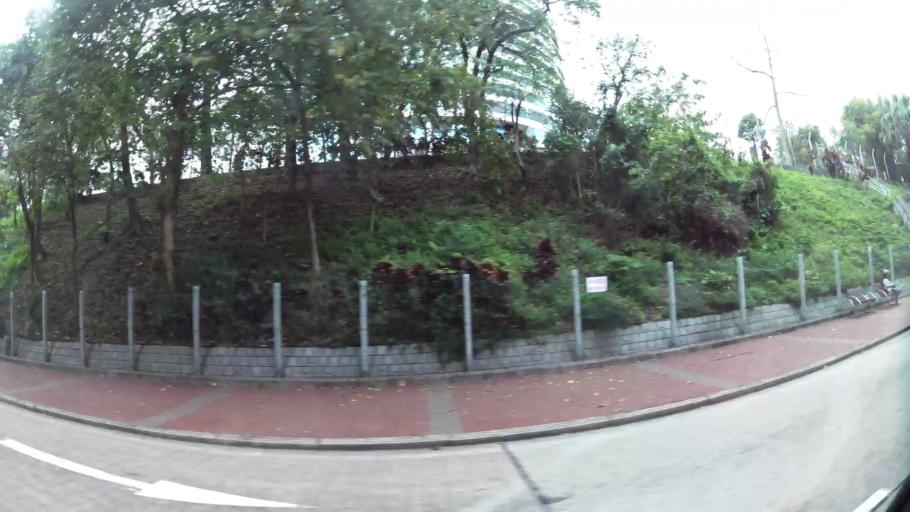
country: HK
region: Sham Shui Po
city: Sham Shui Po
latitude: 22.3229
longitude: 114.1710
